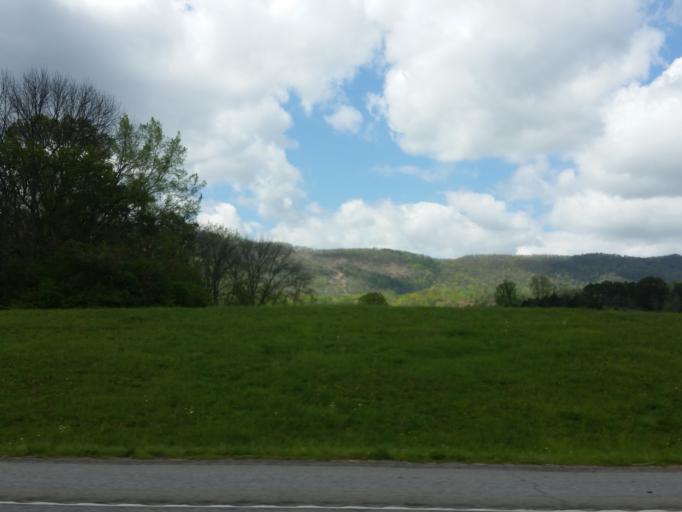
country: US
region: Kentucky
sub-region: Bell County
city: Middlesboro
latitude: 36.5056
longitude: -83.7976
